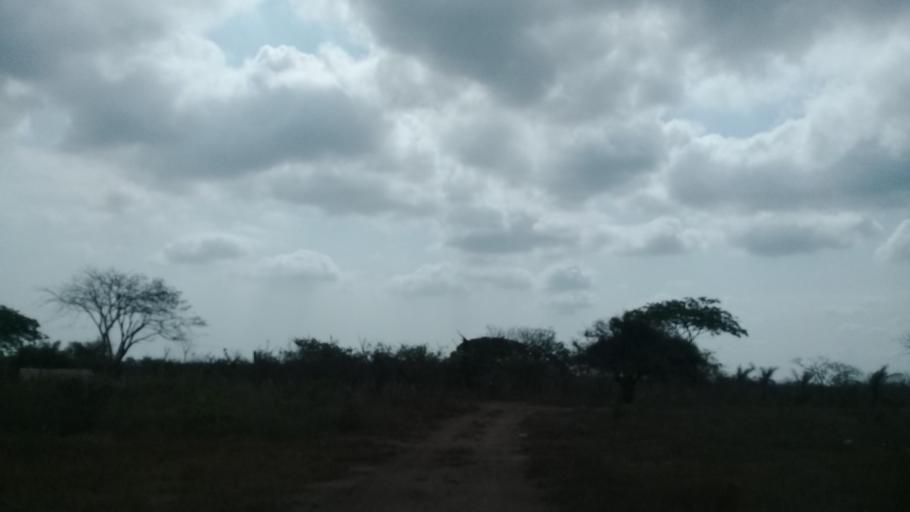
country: MX
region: Veracruz
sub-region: Veracruz
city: Las Amapolas
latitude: 19.1320
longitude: -96.2375
